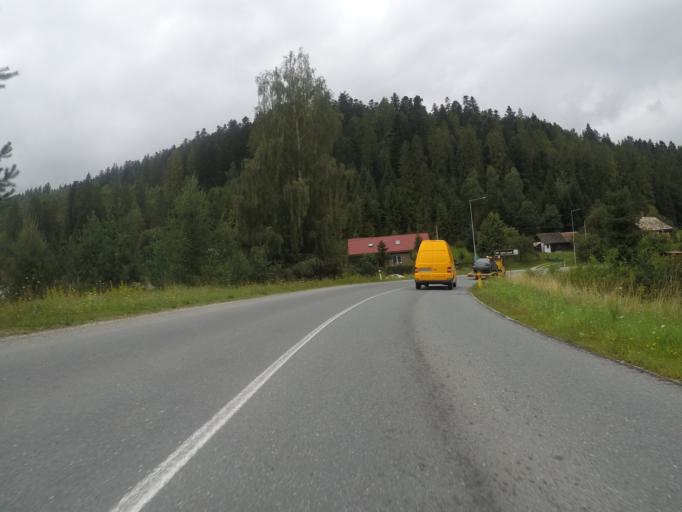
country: SK
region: Kosicky
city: Spisska Nova Ves
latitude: 48.8928
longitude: 20.5197
